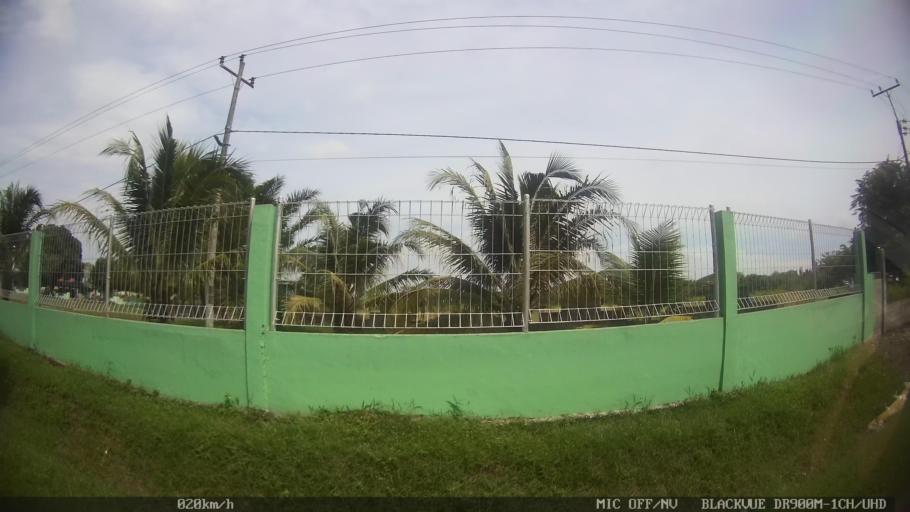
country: ID
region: North Sumatra
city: Medan
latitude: 3.6288
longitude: 98.7156
